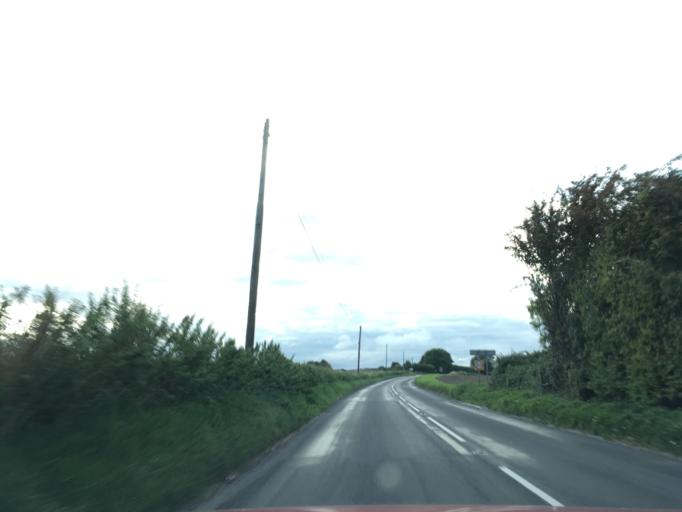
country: GB
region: England
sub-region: Wiltshire
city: Market Lavington
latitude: 51.3175
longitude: -1.9196
